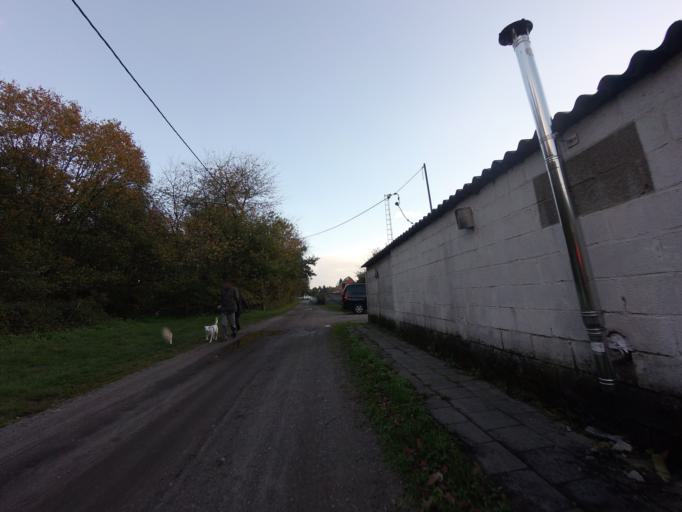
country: BE
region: Flanders
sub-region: Provincie Antwerpen
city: Bonheiden
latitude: 51.0318
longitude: 4.5780
